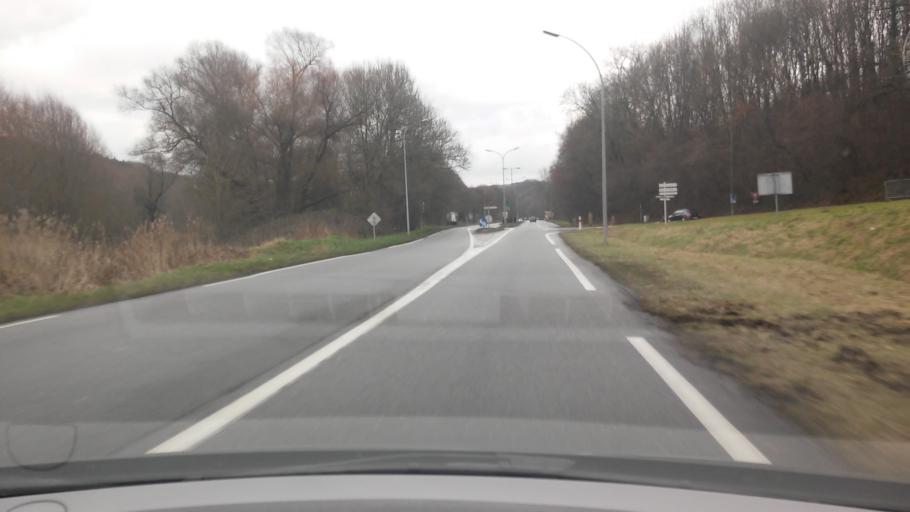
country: FR
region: Lorraine
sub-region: Departement de la Moselle
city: Saint-Avold
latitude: 49.1094
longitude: 6.7262
